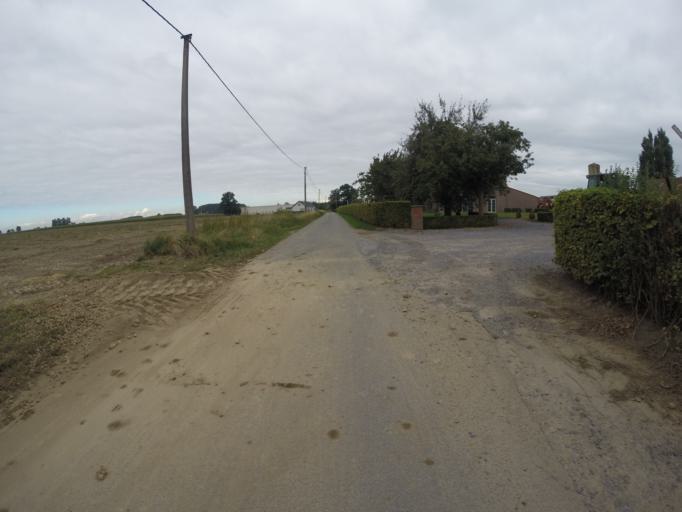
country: BE
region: Flanders
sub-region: Provincie West-Vlaanderen
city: Ruiselede
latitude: 51.0480
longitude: 3.3632
